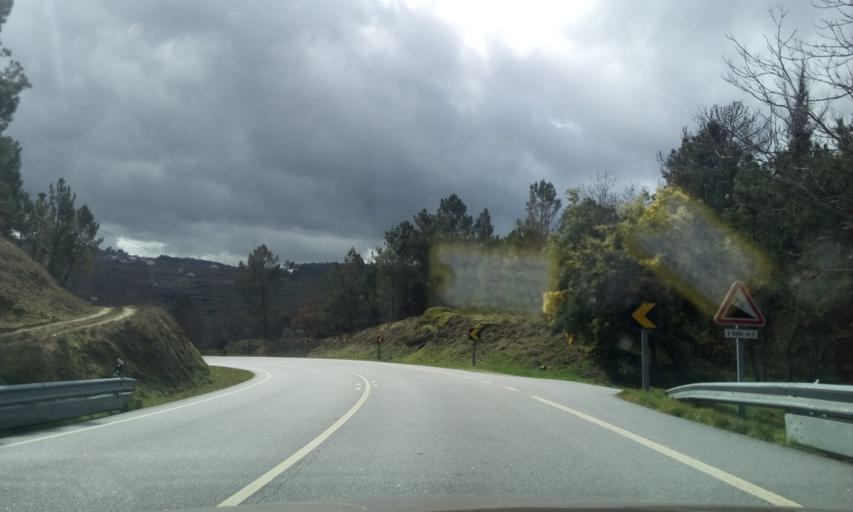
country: PT
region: Viseu
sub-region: Mangualde
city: Mangualde
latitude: 40.6491
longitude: -7.7334
